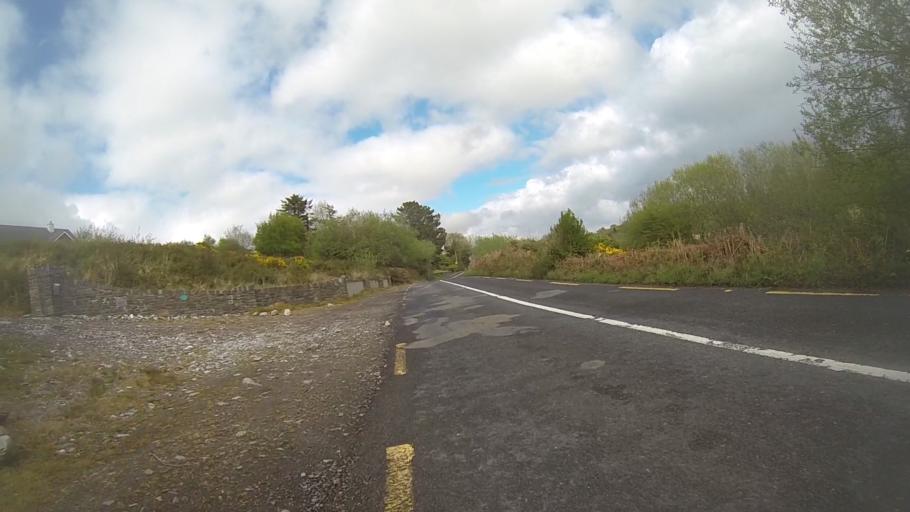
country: IE
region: Munster
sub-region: Ciarrai
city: Kenmare
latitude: 51.8266
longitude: -9.8413
